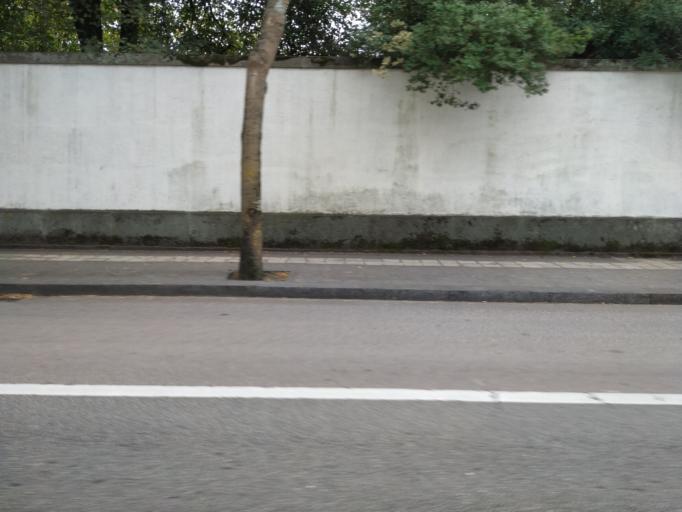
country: PT
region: Porto
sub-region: Porto
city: Porto
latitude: 41.1534
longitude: -8.6400
